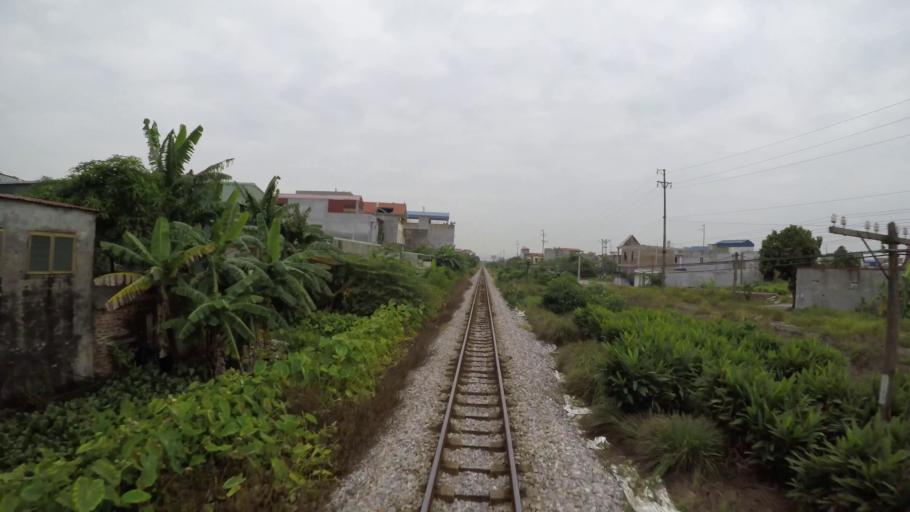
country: VN
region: Hai Duong
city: Phu Thai
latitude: 20.9163
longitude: 106.5638
